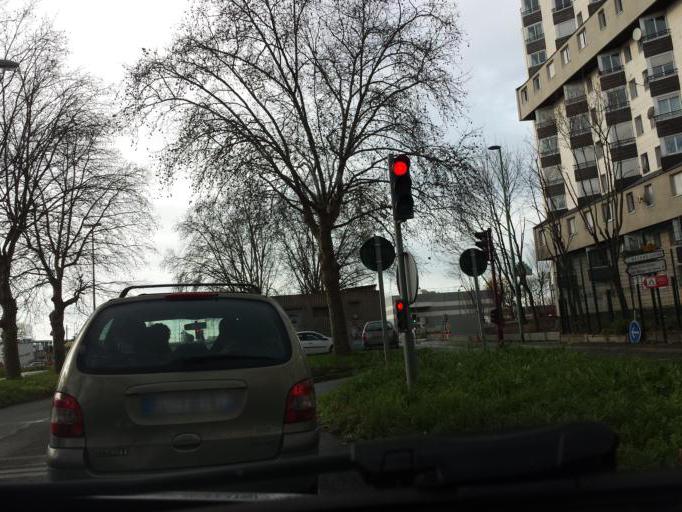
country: FR
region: Ile-de-France
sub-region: Departement du Val-d'Oise
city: Bezons
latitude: 48.9231
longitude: 2.2212
